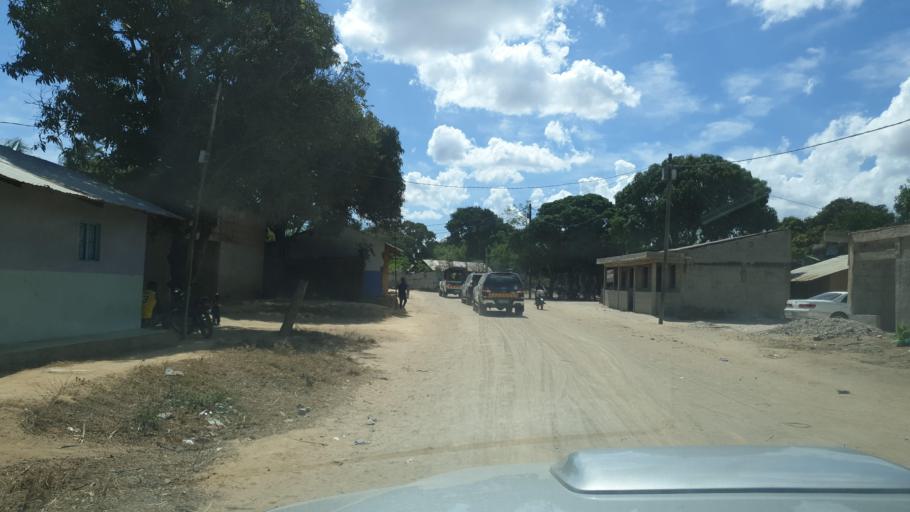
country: MZ
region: Nampula
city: Nacala
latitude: -14.5717
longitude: 40.6865
